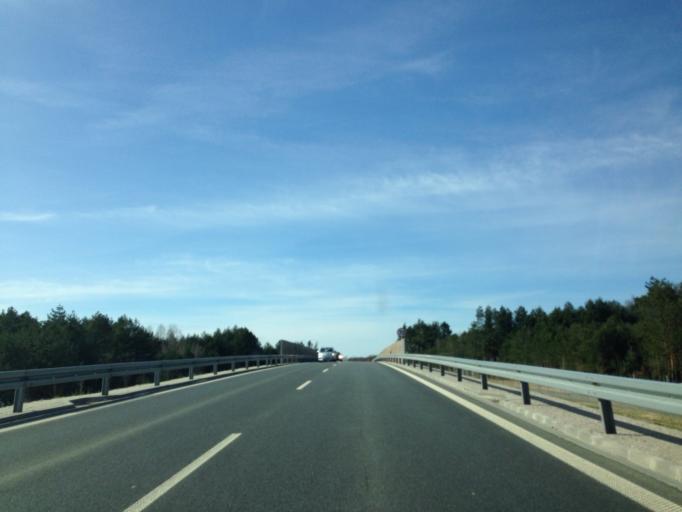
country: PL
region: Lodz Voivodeship
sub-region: Powiat sieradzki
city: Sieradz
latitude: 51.5993
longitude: 18.8169
